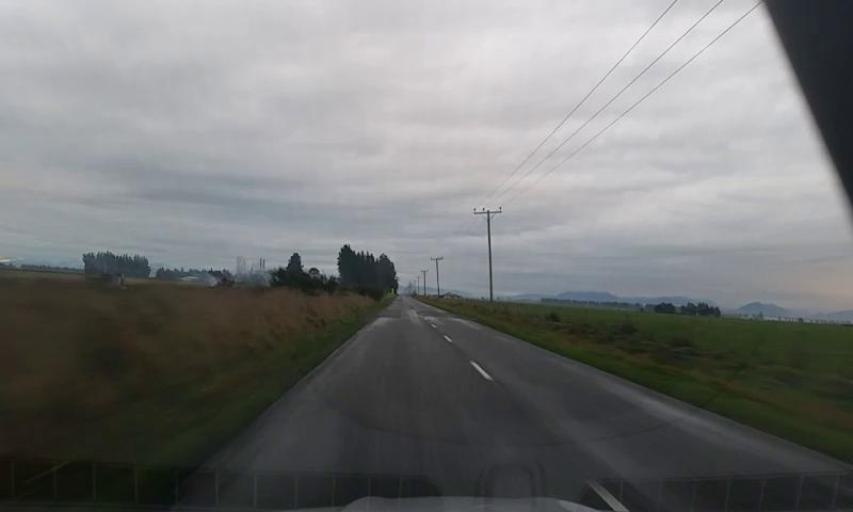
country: NZ
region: Canterbury
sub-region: Ashburton District
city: Ashburton
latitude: -43.7505
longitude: 171.8315
